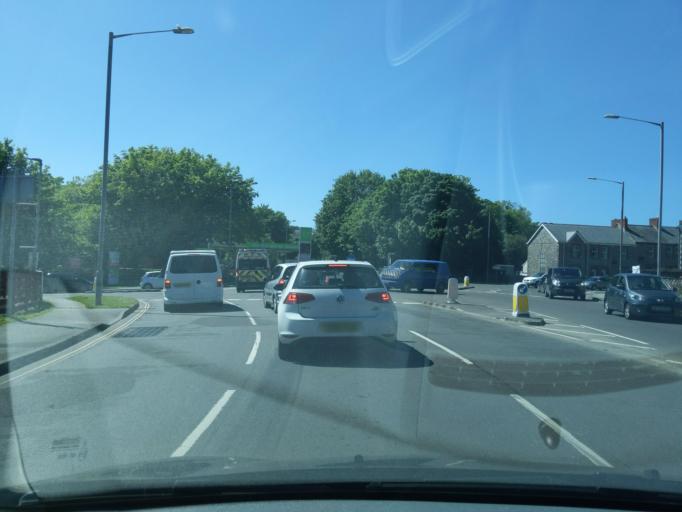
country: GB
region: England
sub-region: Cornwall
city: St Austell
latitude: 50.3343
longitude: -4.7932
